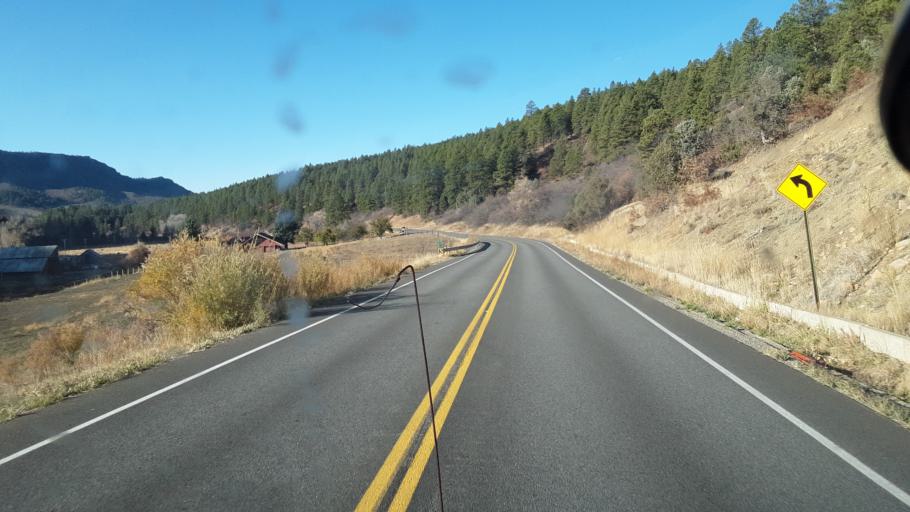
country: US
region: Colorado
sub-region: La Plata County
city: Bayfield
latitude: 37.3455
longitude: -107.7150
